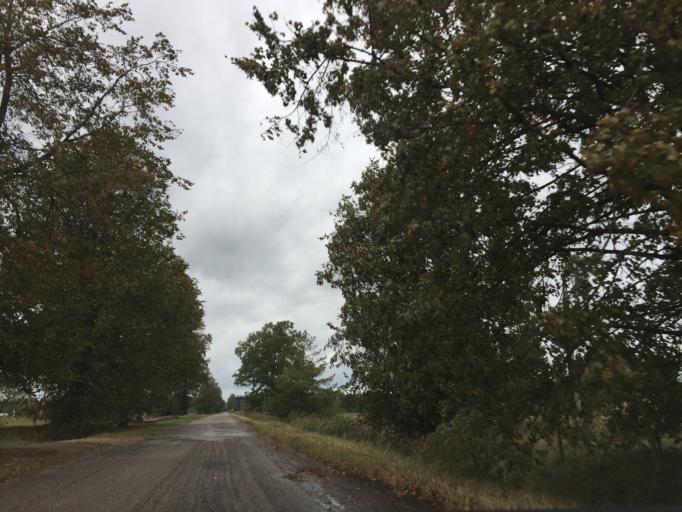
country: LV
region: Olaine
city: Olaine
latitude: 56.7668
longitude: 23.8810
